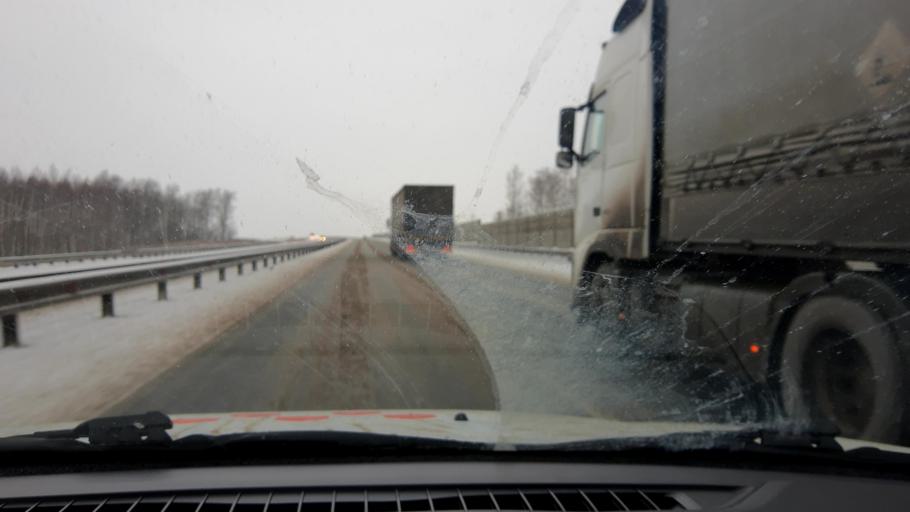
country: RU
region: Nizjnij Novgorod
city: Burevestnik
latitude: 56.1147
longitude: 43.9608
